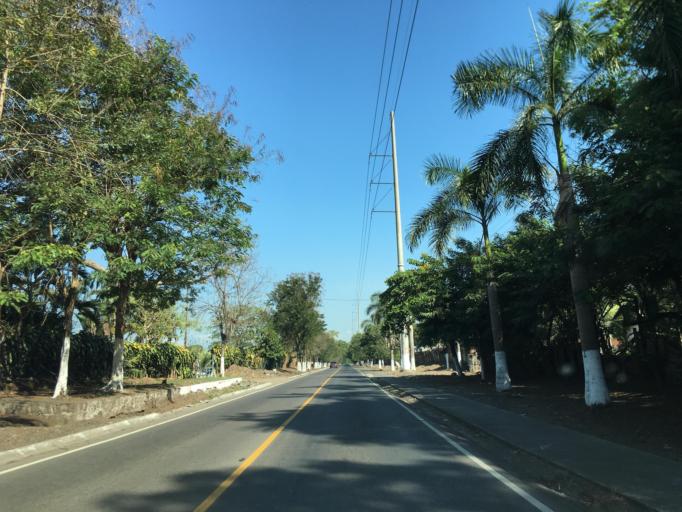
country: GT
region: Escuintla
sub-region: Municipio de La Democracia
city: La Democracia
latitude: 14.2407
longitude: -90.9555
